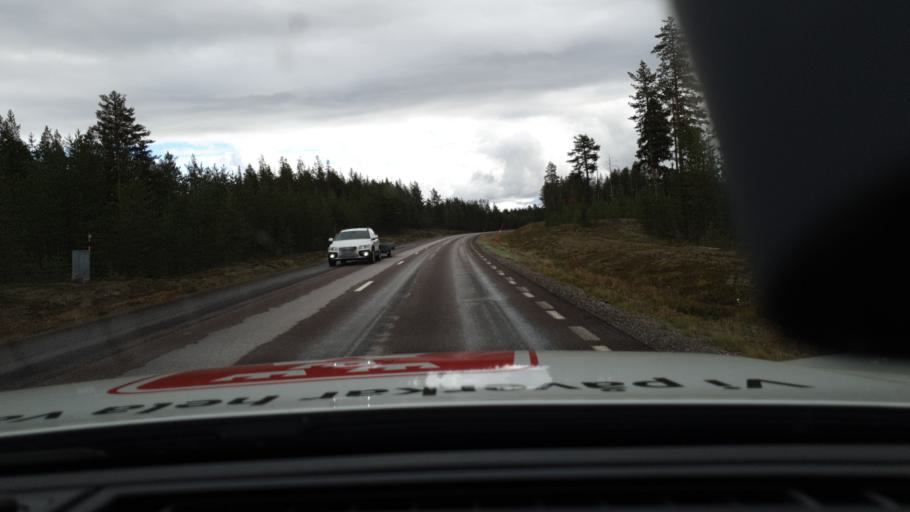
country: SE
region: Norrbotten
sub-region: Gallivare Kommun
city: Gaellivare
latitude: 66.9360
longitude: 21.4603
